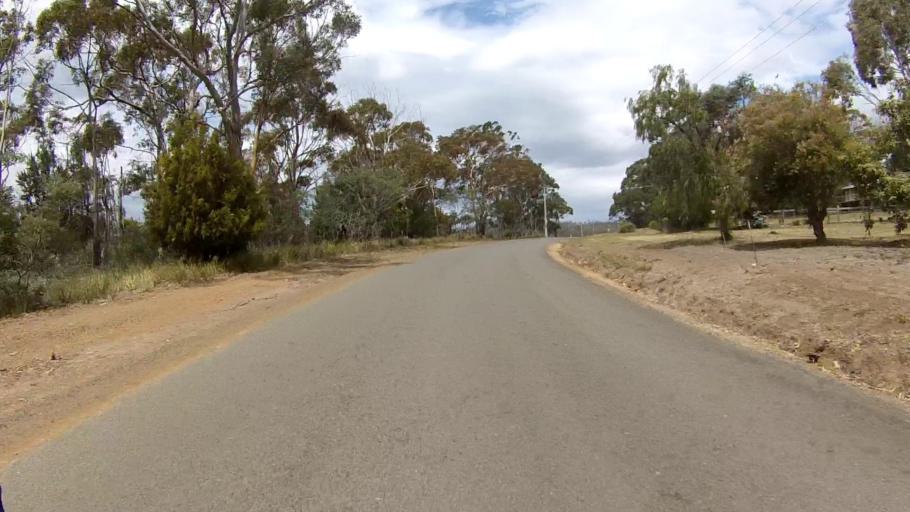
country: AU
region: Tasmania
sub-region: Sorell
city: Sorell
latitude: -42.5862
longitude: 147.9144
